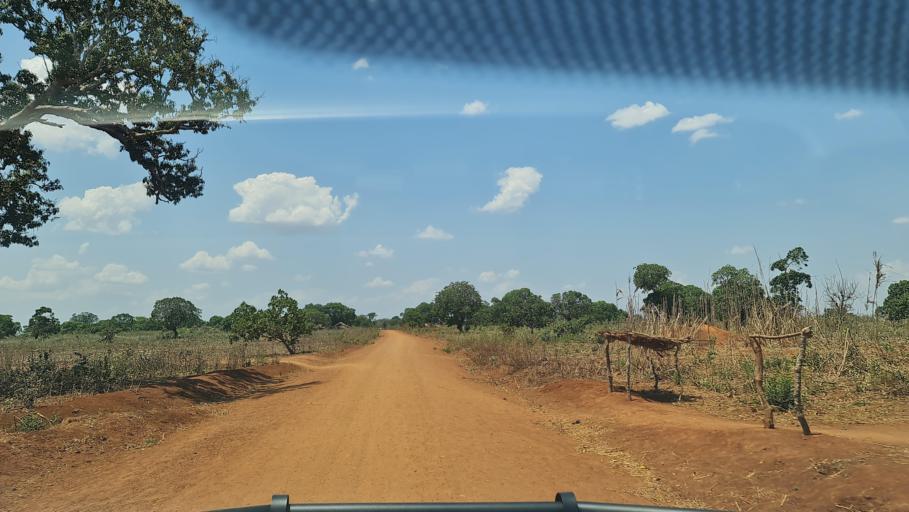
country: MZ
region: Nampula
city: Nacala
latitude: -14.7920
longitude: 40.0664
